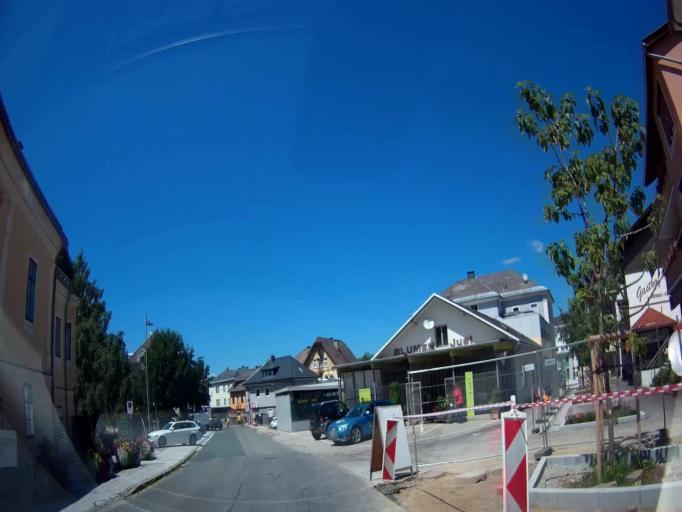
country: AT
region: Carinthia
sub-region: Politischer Bezirk Klagenfurt Land
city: Ferlach
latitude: 46.5257
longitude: 14.3002
